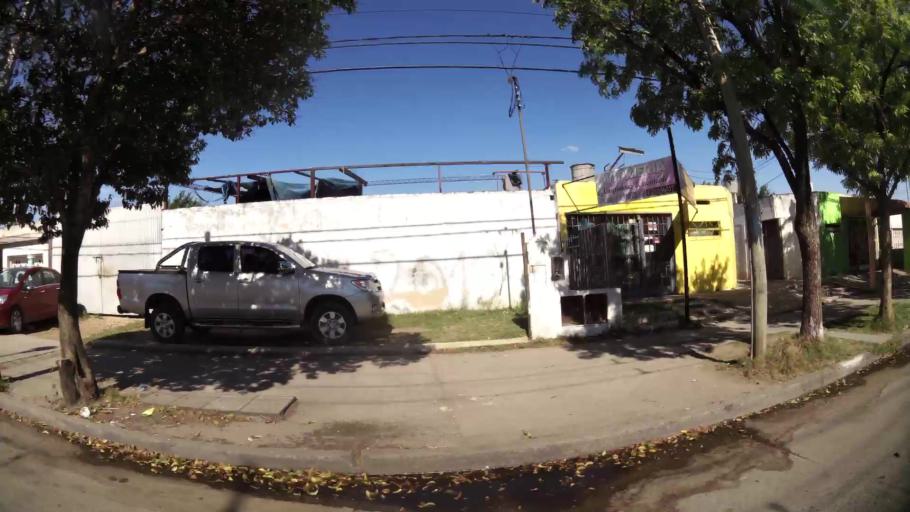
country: AR
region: Cordoba
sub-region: Departamento de Capital
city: Cordoba
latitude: -31.3739
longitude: -64.1838
